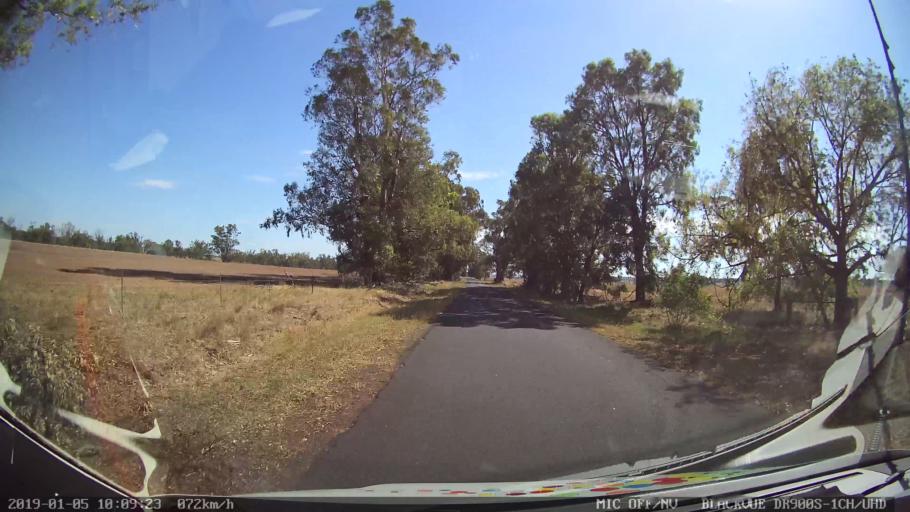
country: AU
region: New South Wales
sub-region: Gilgandra
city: Gilgandra
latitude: -31.6319
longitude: 148.8863
